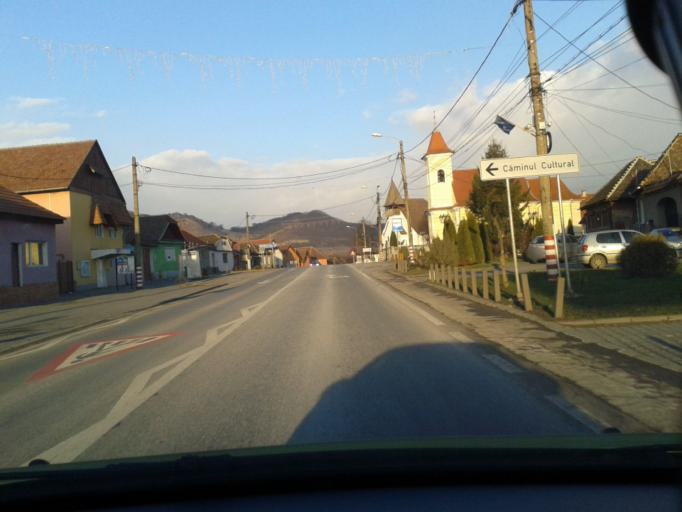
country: RO
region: Sibiu
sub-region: Comuna Copsa Mica
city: Copsa Mica
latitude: 46.1153
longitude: 24.2526
